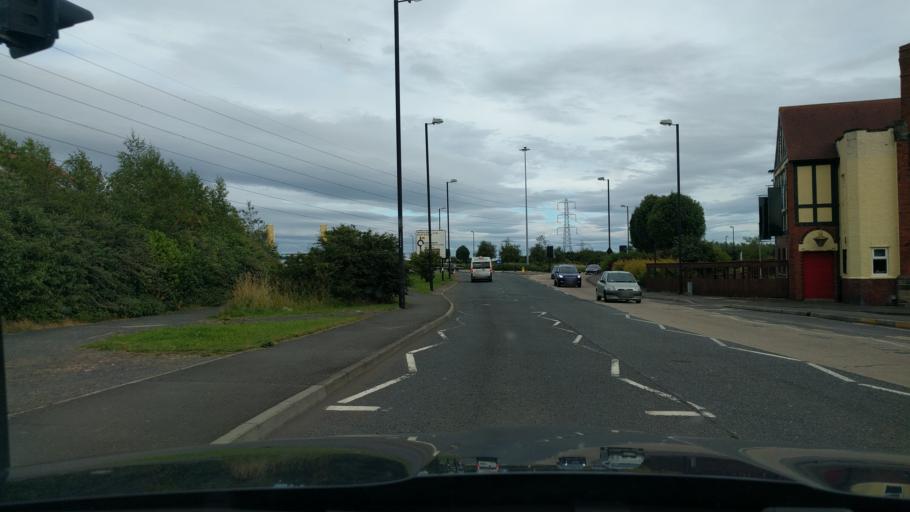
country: GB
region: England
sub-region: Borough of North Tyneside
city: Shiremoor
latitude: 55.0290
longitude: -1.5114
